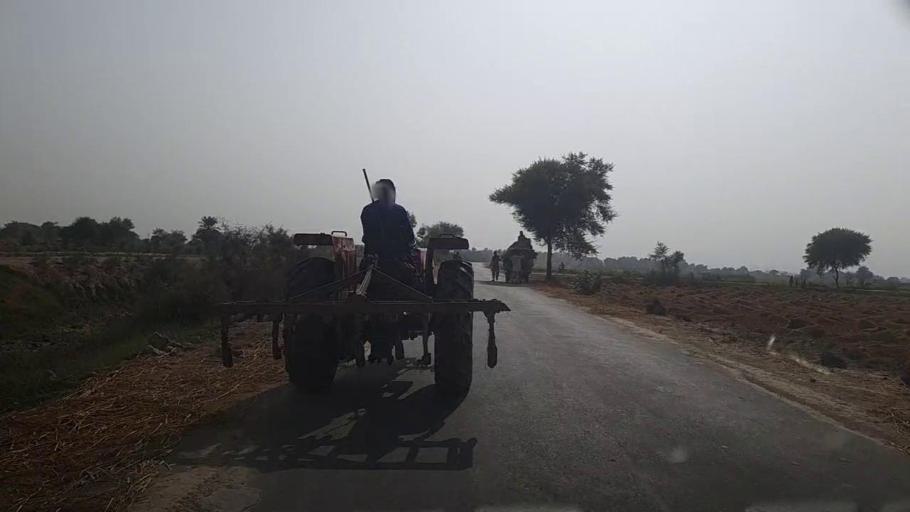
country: PK
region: Sindh
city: Kashmor
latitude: 28.4146
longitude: 69.5674
